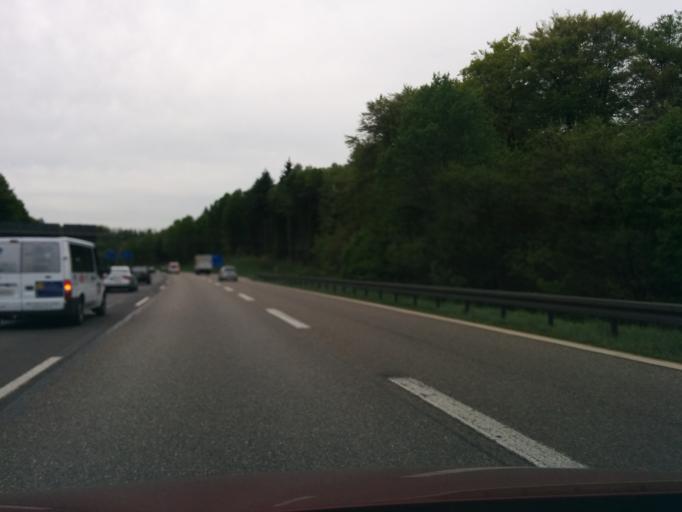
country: DE
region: Baden-Wuerttemberg
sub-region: Regierungsbezirk Stuttgart
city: Sindelfingen
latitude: 48.7212
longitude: 9.0584
